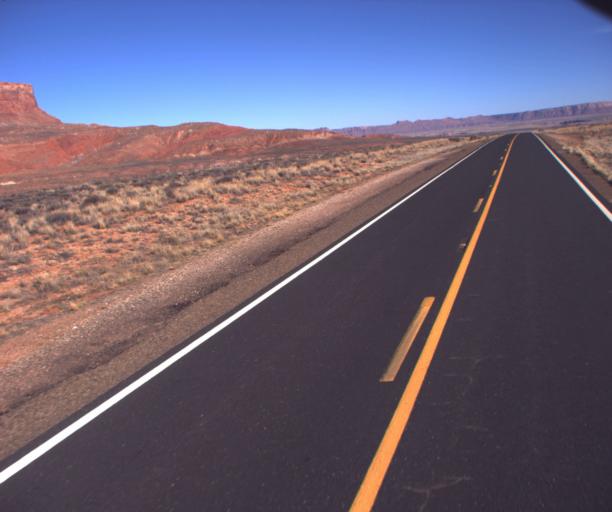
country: US
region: Arizona
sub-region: Coconino County
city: Page
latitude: 36.6911
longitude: -111.8877
